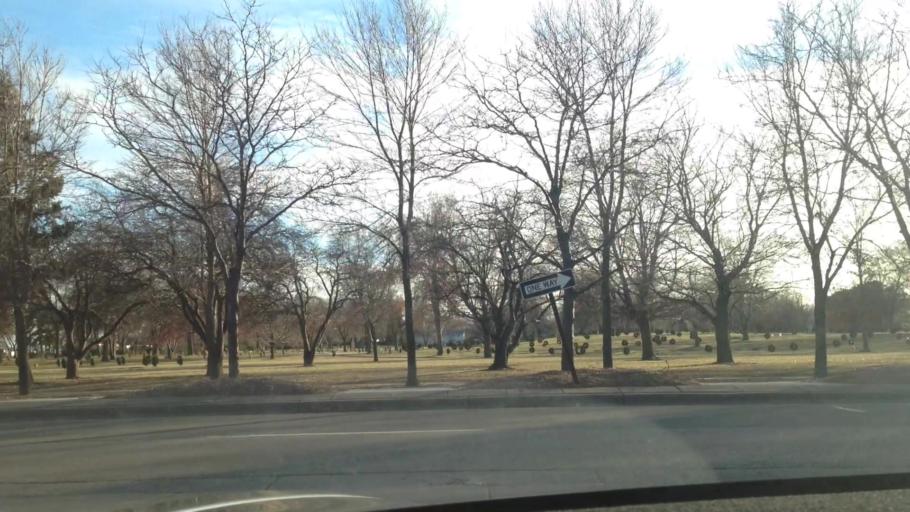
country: US
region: Minnesota
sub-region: Hennepin County
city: New Hope
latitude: 45.0330
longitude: -93.3814
